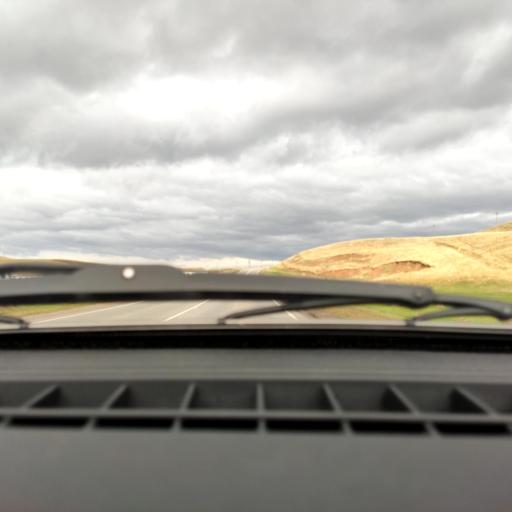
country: RU
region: Bashkortostan
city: Rayevskiy
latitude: 54.0158
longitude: 54.8768
